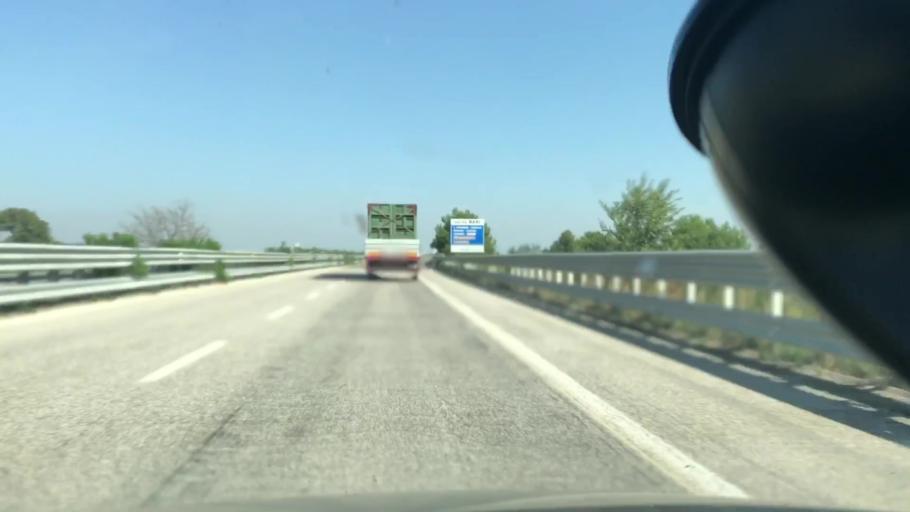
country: IT
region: Apulia
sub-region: Provincia di Foggia
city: Foggia
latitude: 41.4180
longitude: 15.5587
